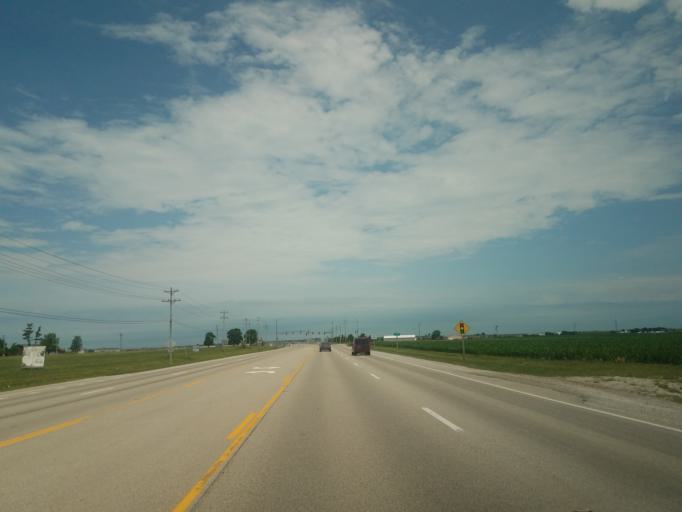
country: US
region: Illinois
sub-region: McLean County
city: Downs
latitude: 40.4703
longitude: -88.9021
